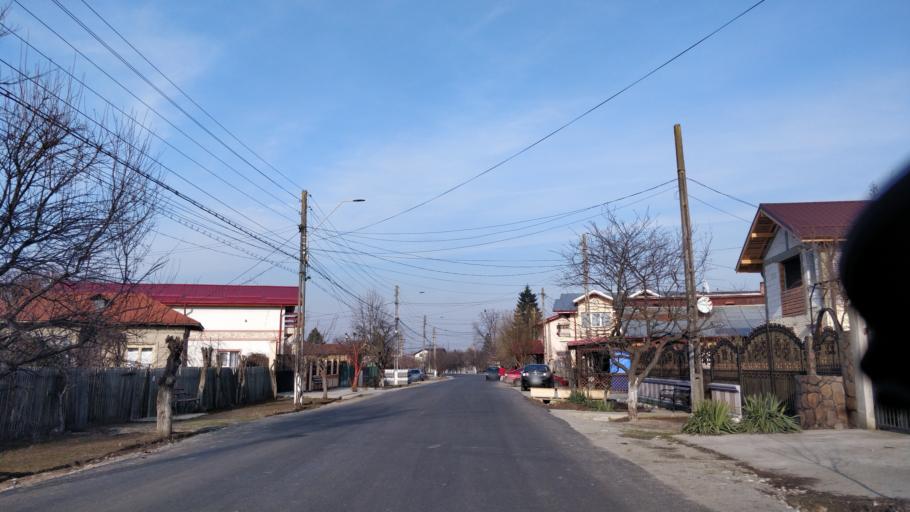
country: RO
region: Giurgiu
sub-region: Comuna Ulmi
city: Trestieni
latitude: 44.5081
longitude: 25.7624
